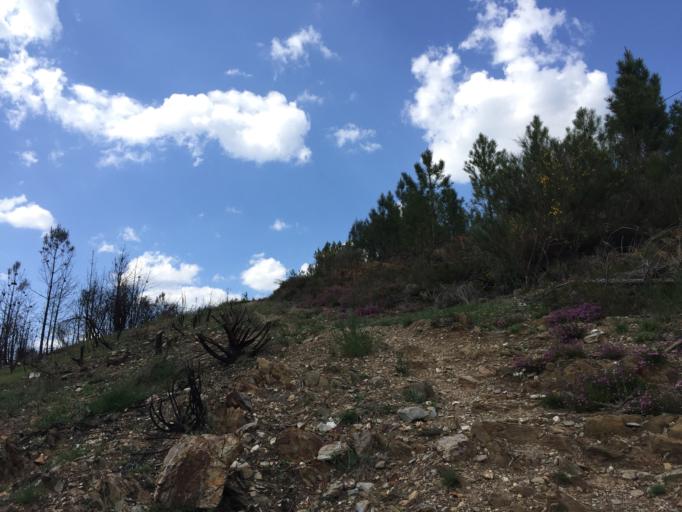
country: PT
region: Coimbra
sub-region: Pampilhosa da Serra
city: Pampilhosa da Serra
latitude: 40.1022
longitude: -7.8660
